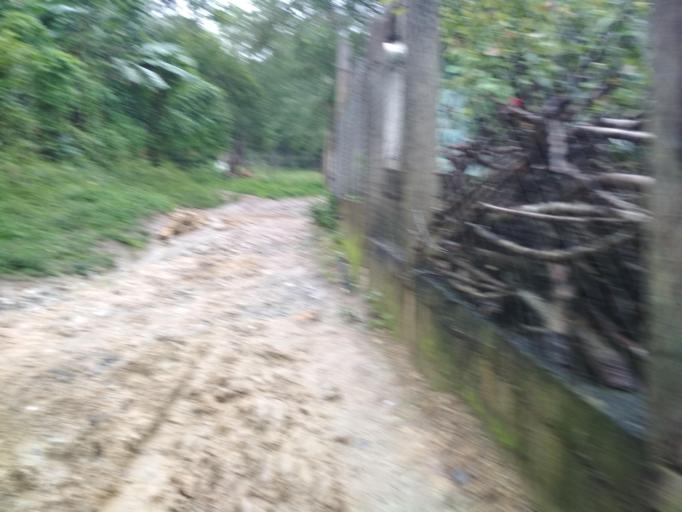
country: MX
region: Veracruz
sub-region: Chalma
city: San Pedro Coyutla
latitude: 21.1863
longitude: -98.4332
